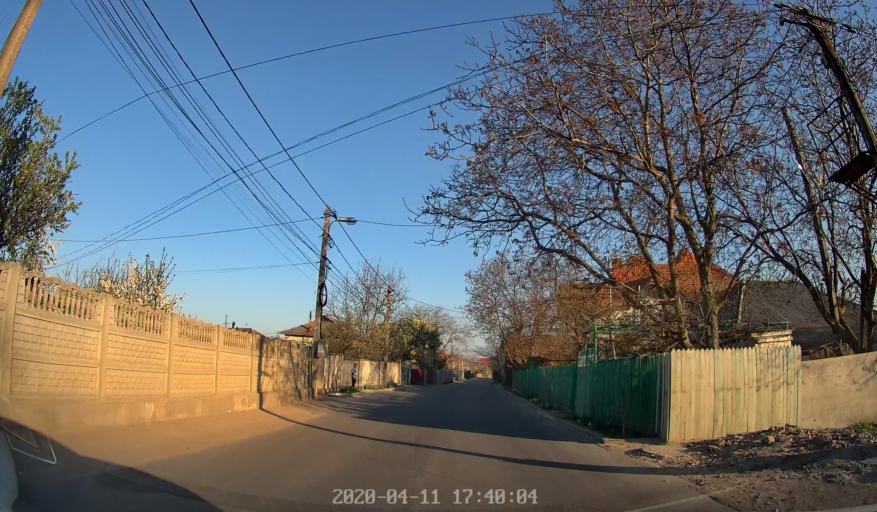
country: MD
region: Laloveni
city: Ialoveni
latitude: 46.9810
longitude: 28.8091
